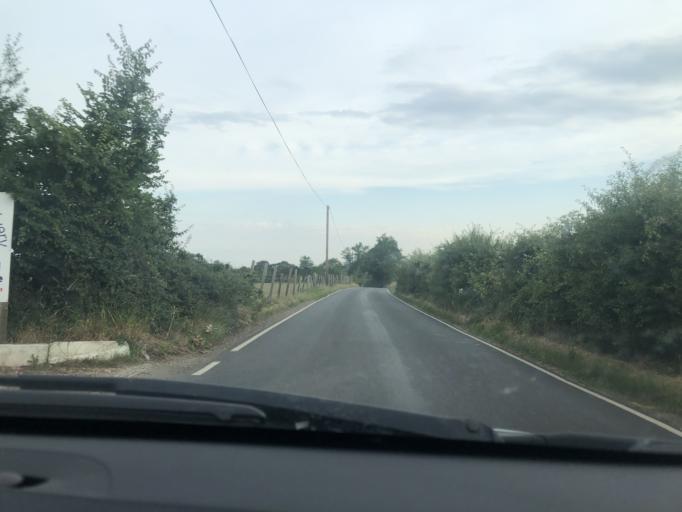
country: GB
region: England
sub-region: Kent
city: Herne Bay
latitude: 51.3361
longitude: 1.1561
